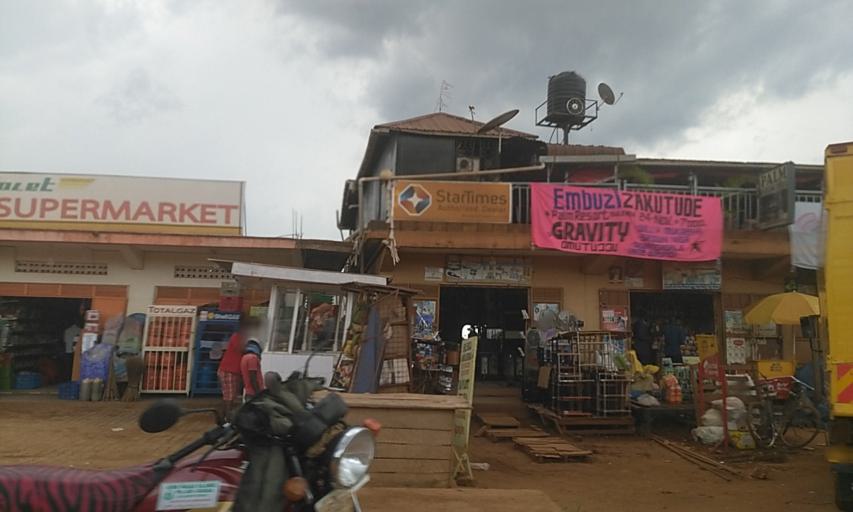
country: UG
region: Central Region
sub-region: Wakiso District
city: Wakiso
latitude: 0.3329
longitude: 32.4909
